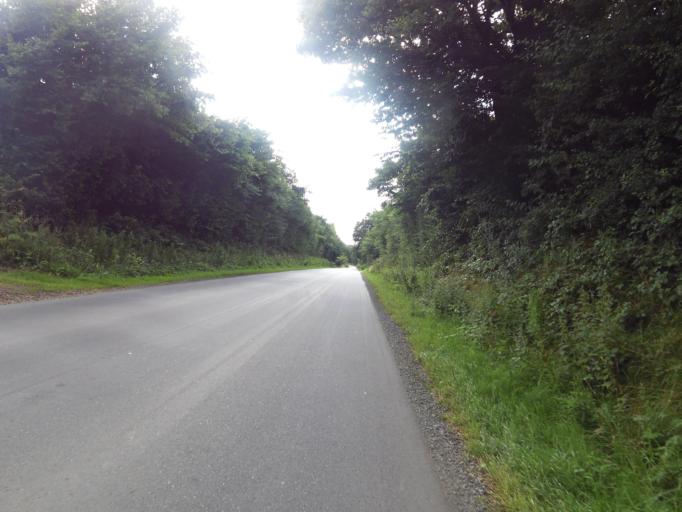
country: DK
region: South Denmark
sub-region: Haderslev Kommune
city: Haderslev
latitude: 55.2067
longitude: 9.4168
